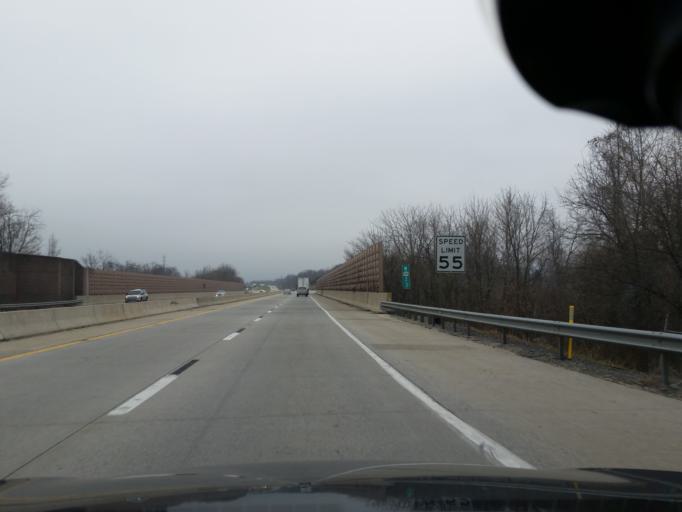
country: US
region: Pennsylvania
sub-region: Cumberland County
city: Mechanicsburg
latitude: 40.2510
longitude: -76.9869
